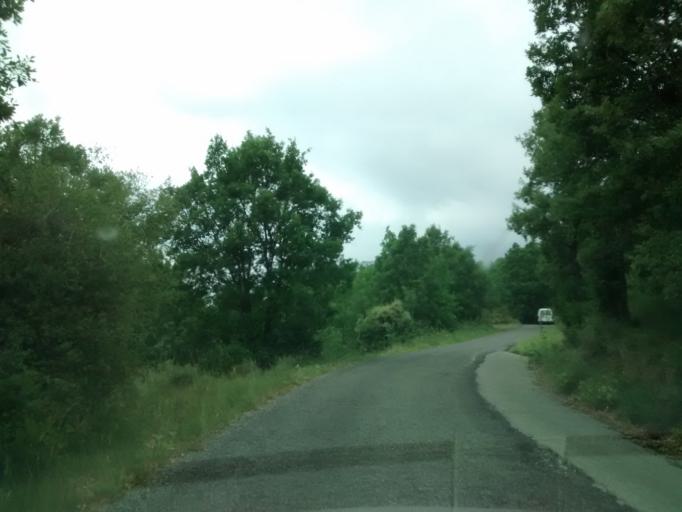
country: ES
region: Aragon
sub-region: Provincia de Huesca
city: Puertolas
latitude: 42.5405
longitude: 0.1311
